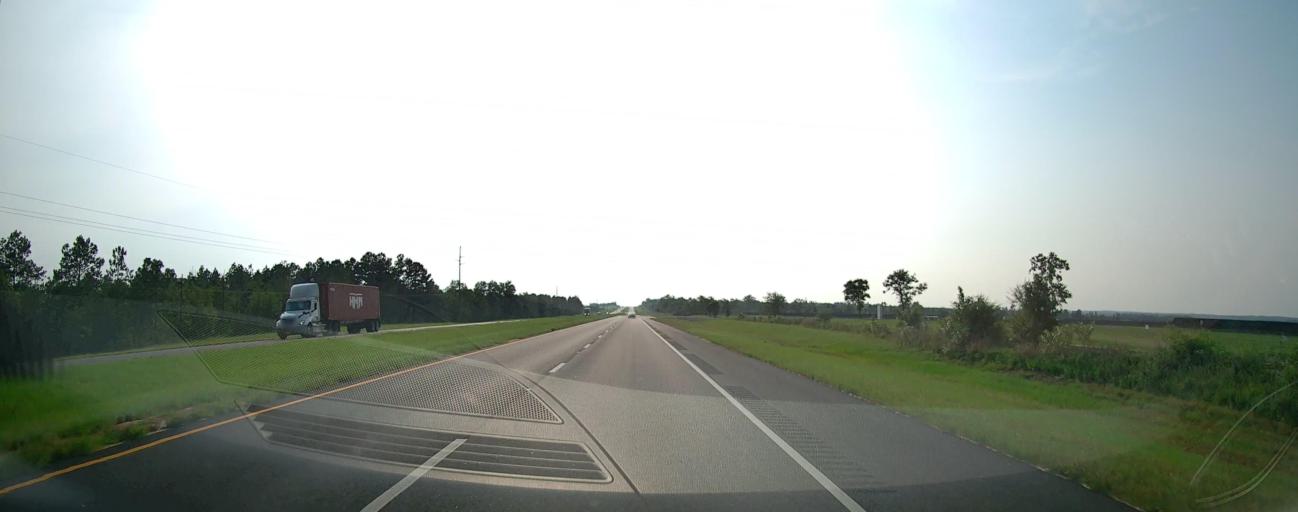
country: US
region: Georgia
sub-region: Taylor County
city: Butler
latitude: 32.5737
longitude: -84.2962
